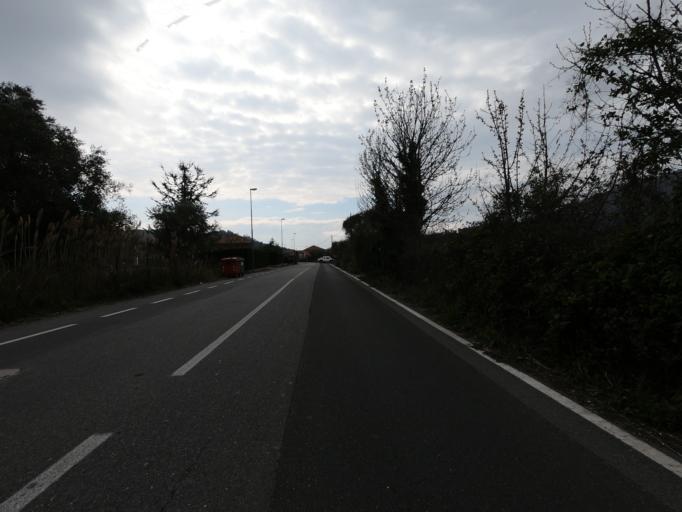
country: IT
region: Liguria
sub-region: Provincia di Savona
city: Andora
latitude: 43.9738
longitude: 8.1373
